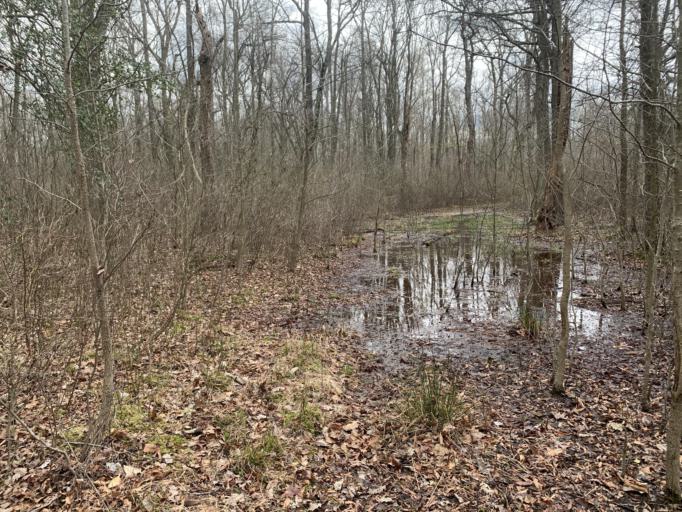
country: US
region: Delaware
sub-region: Kent County
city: Clayton
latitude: 39.1720
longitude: -75.7804
